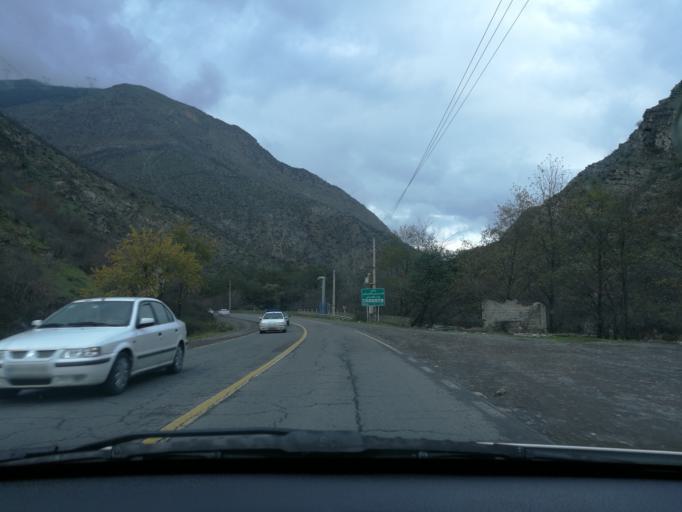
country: IR
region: Mazandaran
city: Chalus
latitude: 36.3441
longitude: 51.2580
